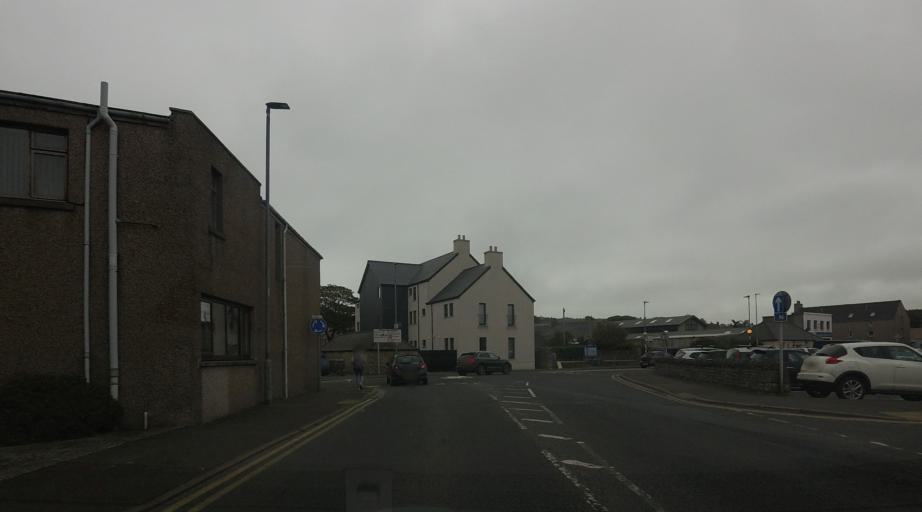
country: GB
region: Scotland
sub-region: Orkney Islands
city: Orkney
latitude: 58.9802
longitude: -2.9638
